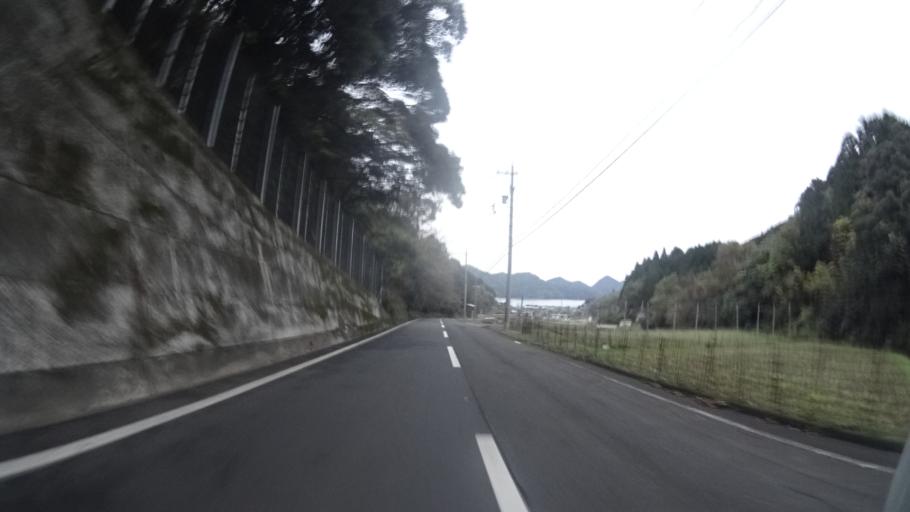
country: JP
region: Kyoto
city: Maizuru
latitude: 35.5608
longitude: 135.4546
